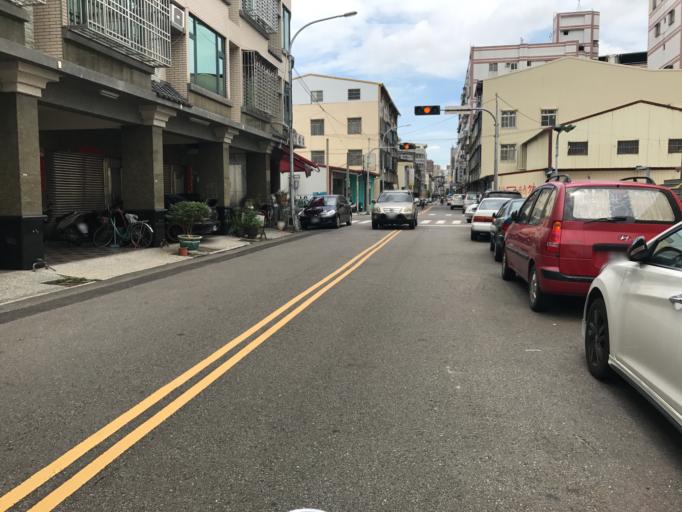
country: TW
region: Taiwan
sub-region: Taichung City
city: Taichung
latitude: 24.0604
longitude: 120.6973
